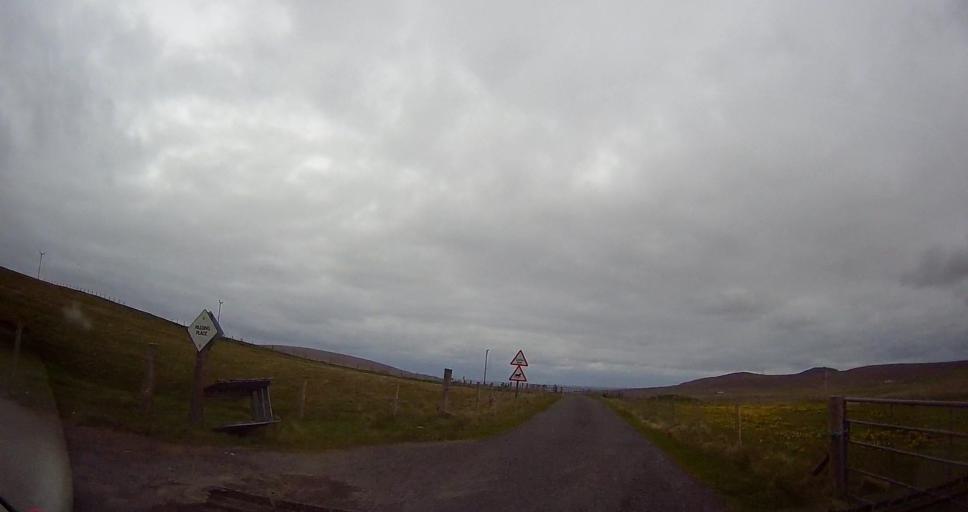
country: GB
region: Scotland
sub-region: Shetland Islands
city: Shetland
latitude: 60.7994
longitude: -0.8719
